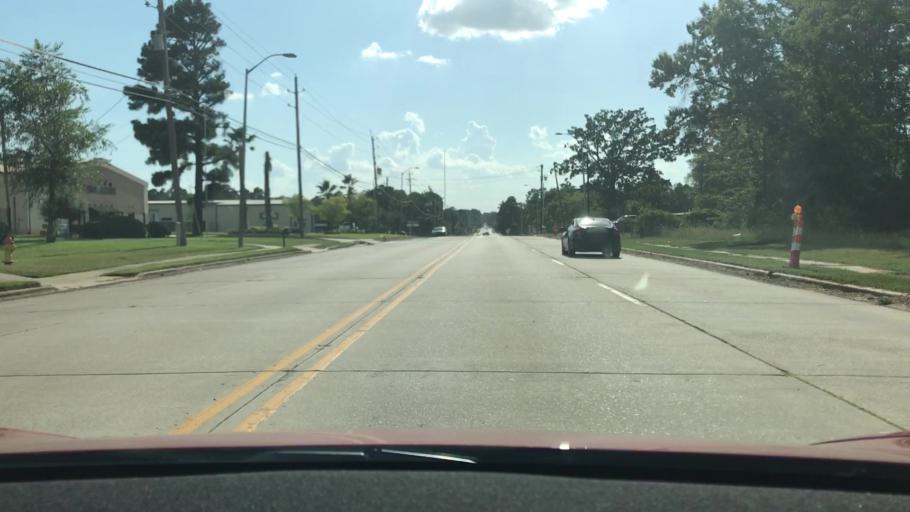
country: US
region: Louisiana
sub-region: Bossier Parish
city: Bossier City
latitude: 32.4130
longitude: -93.7669
